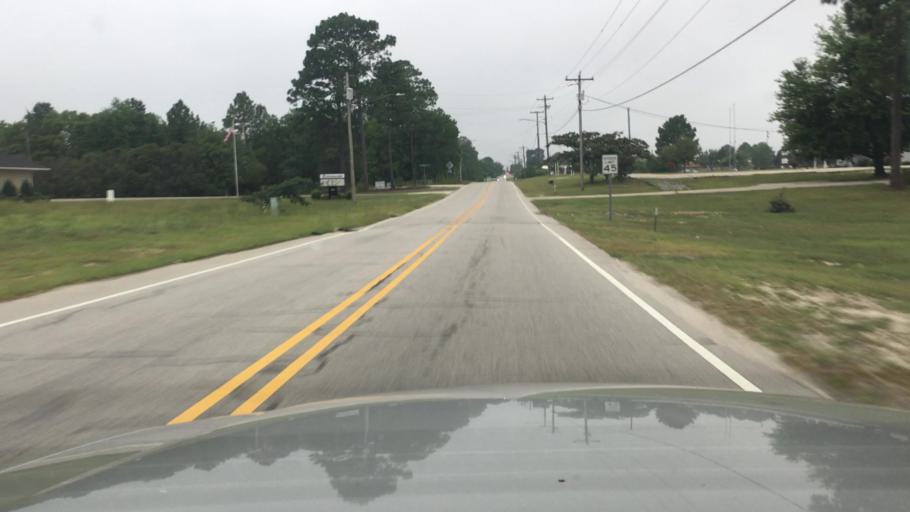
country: US
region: North Carolina
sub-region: Cumberland County
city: Fayetteville
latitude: 35.0118
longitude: -78.8885
